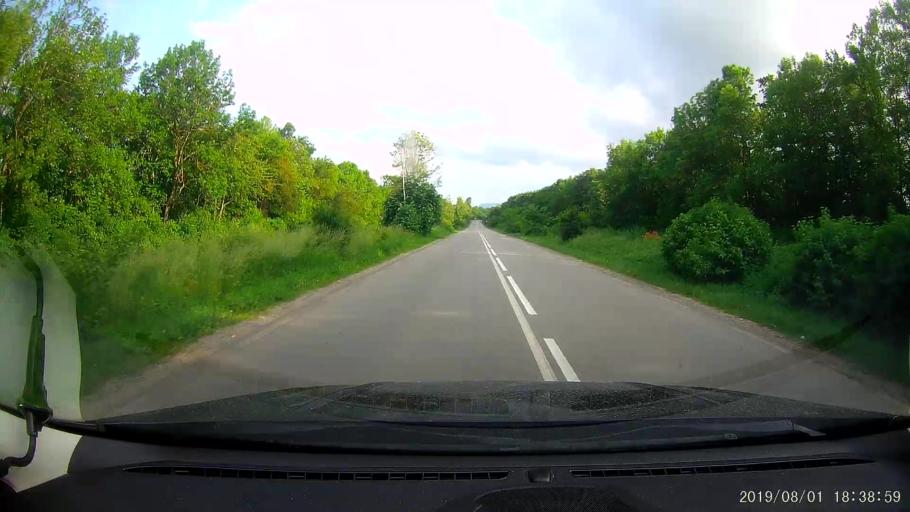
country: BG
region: Shumen
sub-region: Obshtina Khitrino
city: Gara Khitrino
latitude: 43.3948
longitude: 26.9172
